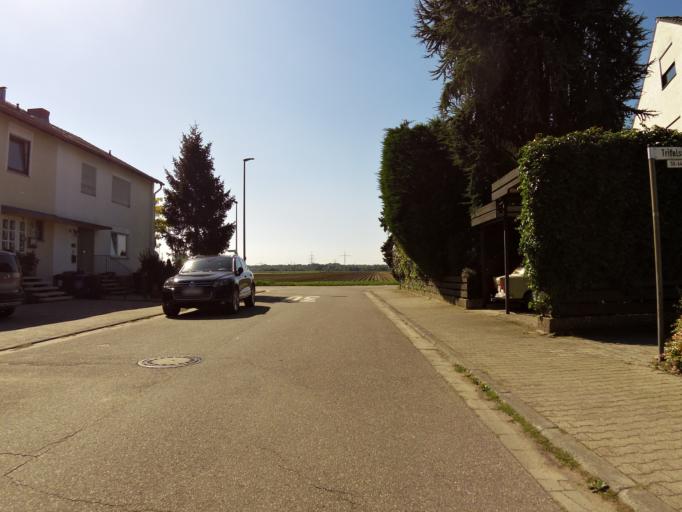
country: DE
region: Rheinland-Pfalz
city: Mutterstadt
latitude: 49.4356
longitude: 8.3487
